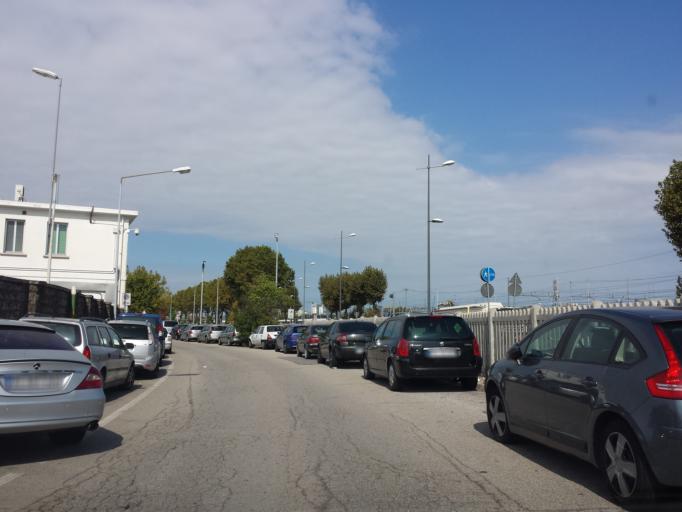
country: IT
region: Veneto
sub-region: Provincia di Venezia
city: Mestre
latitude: 45.4761
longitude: 12.2502
